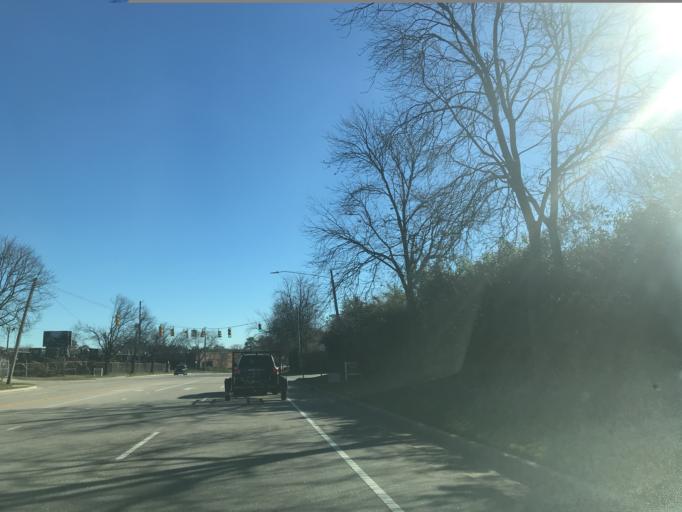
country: US
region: North Carolina
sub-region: Wake County
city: West Raleigh
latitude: 35.7929
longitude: -78.7054
